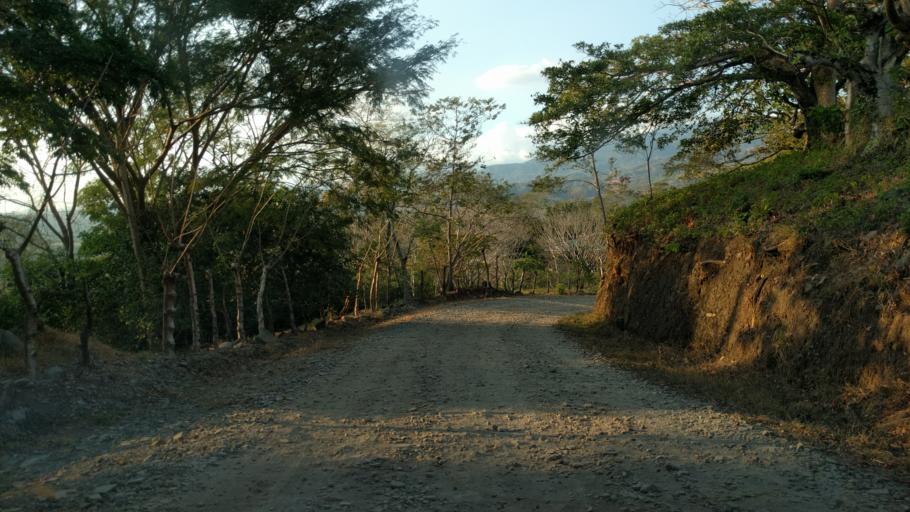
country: CR
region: Puntarenas
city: Esparza
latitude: 10.0287
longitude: -84.6982
